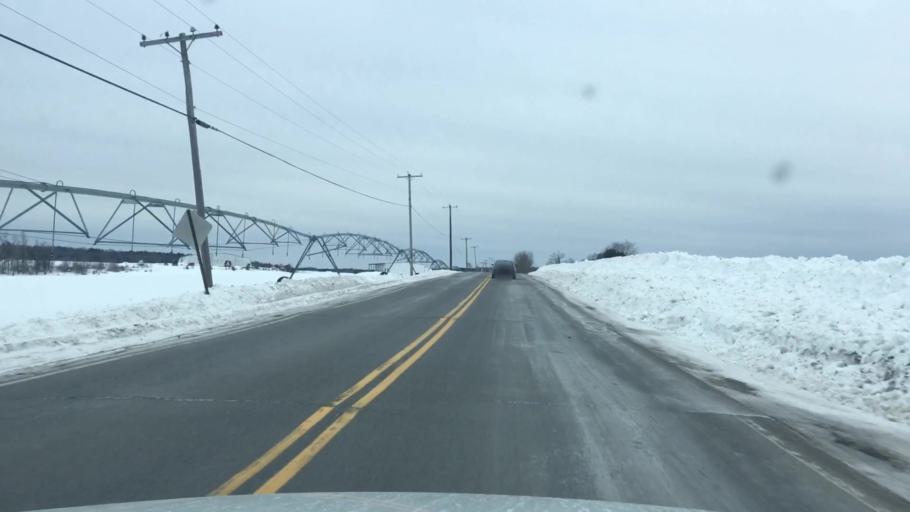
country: US
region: Maine
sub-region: Penobscot County
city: Garland
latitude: 44.9818
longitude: -69.0884
